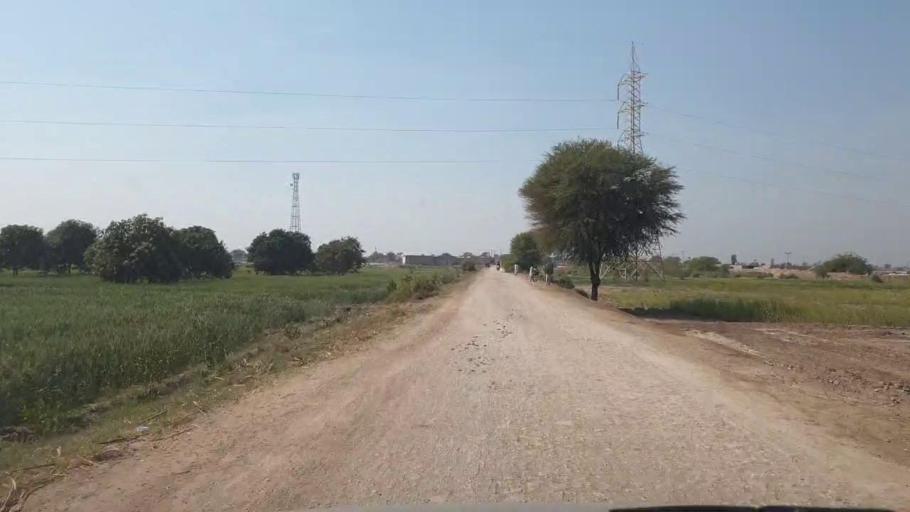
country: PK
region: Sindh
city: Chambar
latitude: 25.3320
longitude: 68.8012
